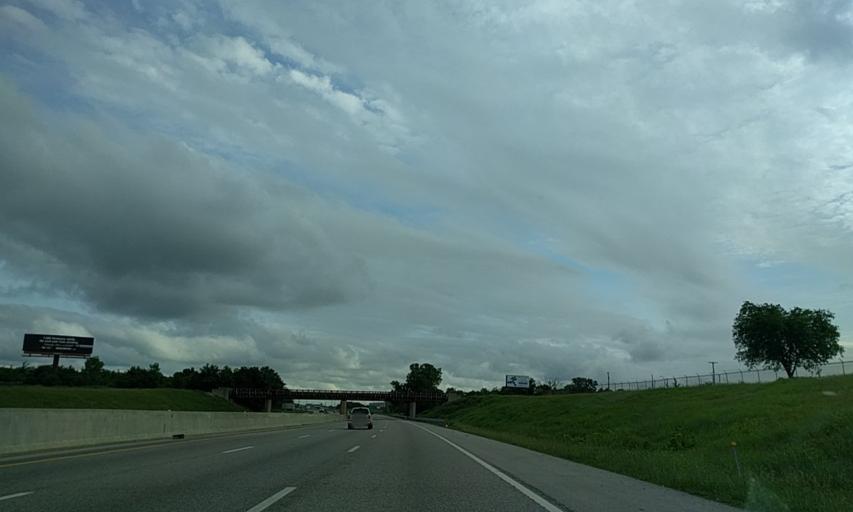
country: US
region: Oklahoma
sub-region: Tulsa County
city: Owasso
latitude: 36.1837
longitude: -95.8525
